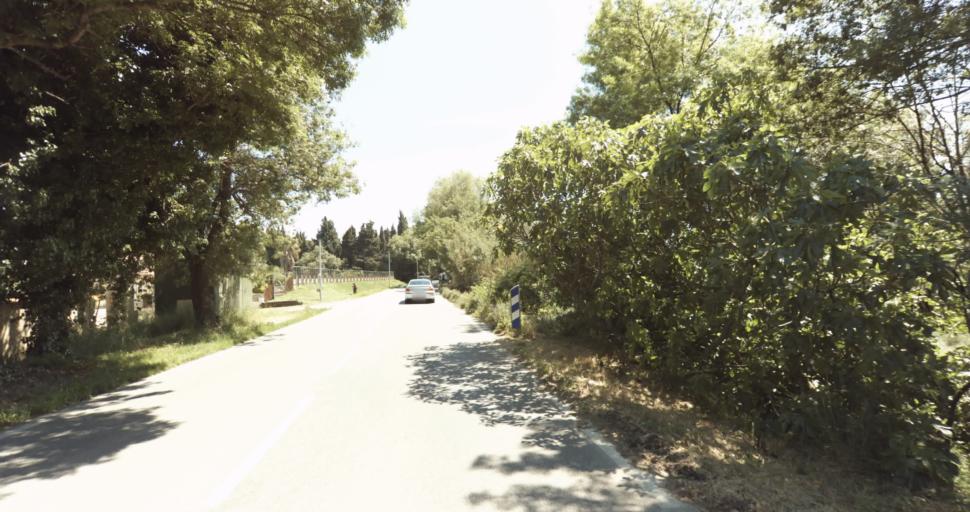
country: FR
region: Provence-Alpes-Cote d'Azur
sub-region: Departement du Var
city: Hyeres
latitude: 43.1328
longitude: 6.1629
